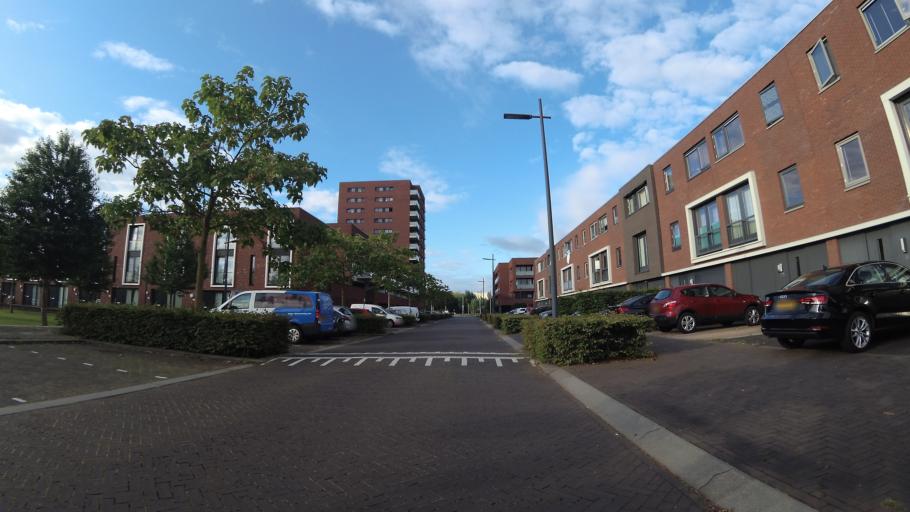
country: NL
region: North Brabant
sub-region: Gemeente Breda
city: Hoge Vucht
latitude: 51.6090
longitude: 4.8023
